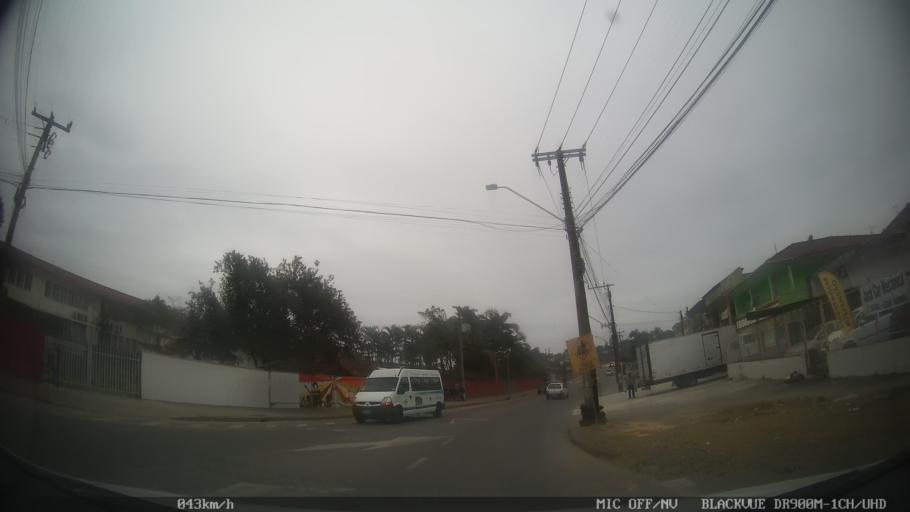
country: BR
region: Santa Catarina
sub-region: Joinville
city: Joinville
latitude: -26.3522
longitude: -48.8201
